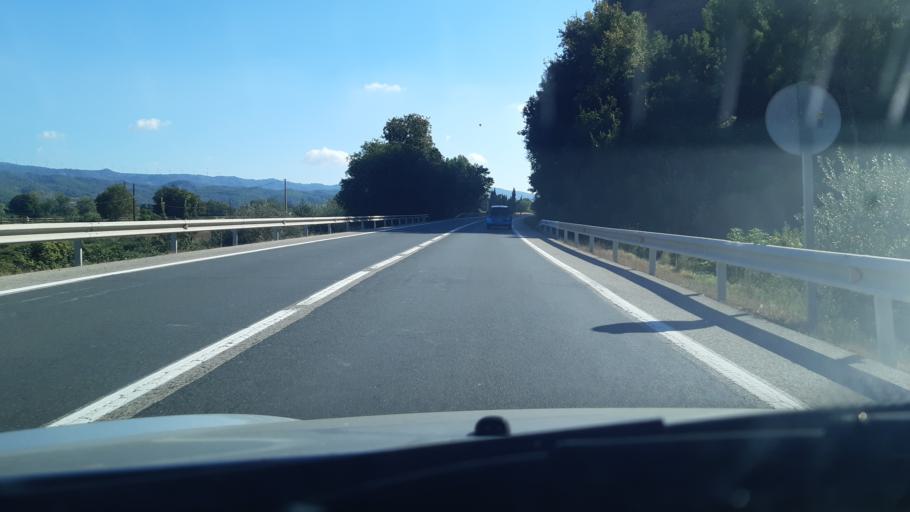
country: ES
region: Catalonia
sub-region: Provincia de Tarragona
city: Tivenys
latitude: 40.8689
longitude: 0.5030
